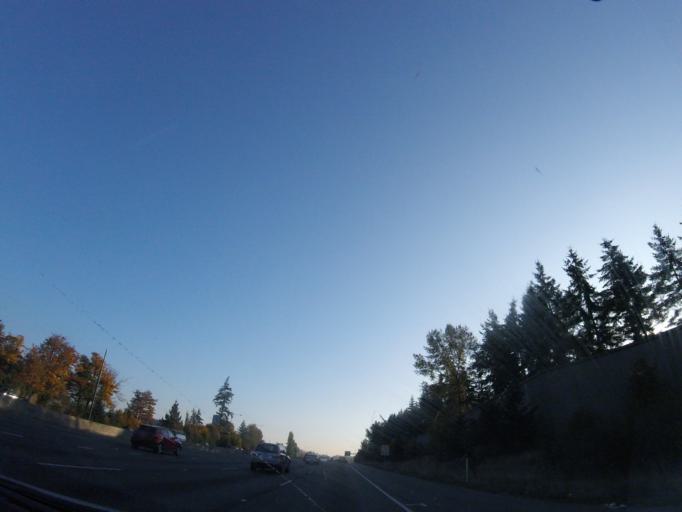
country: US
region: Washington
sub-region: King County
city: Kirkland
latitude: 47.6900
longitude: -122.1823
